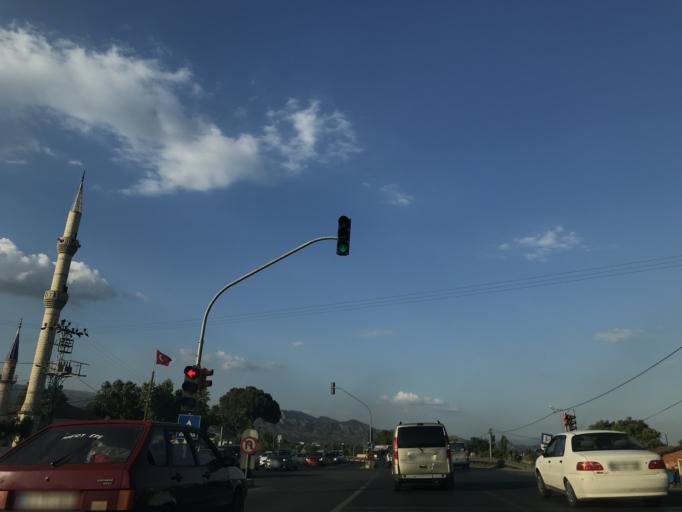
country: TR
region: Aydin
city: Sultanhisar
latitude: 37.8765
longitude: 28.1384
